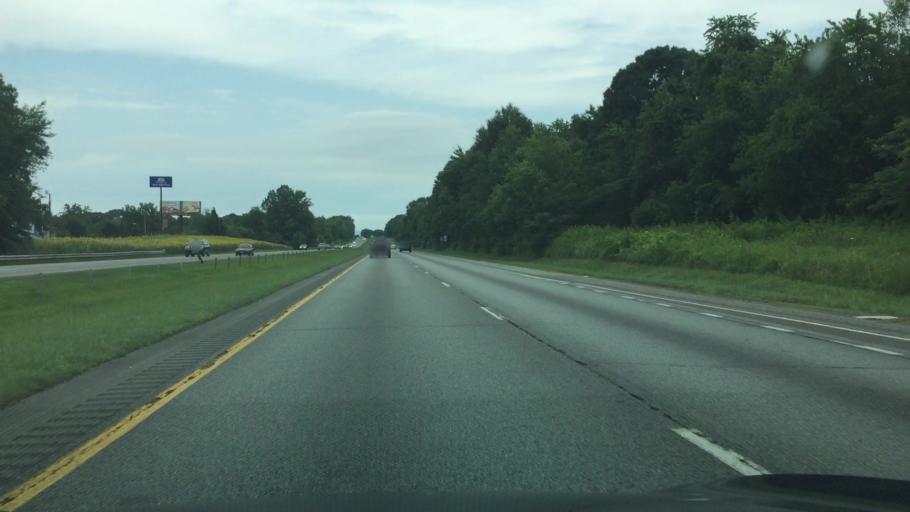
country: US
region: North Carolina
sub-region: Yadkin County
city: Jonesville
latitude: 36.1989
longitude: -80.8113
